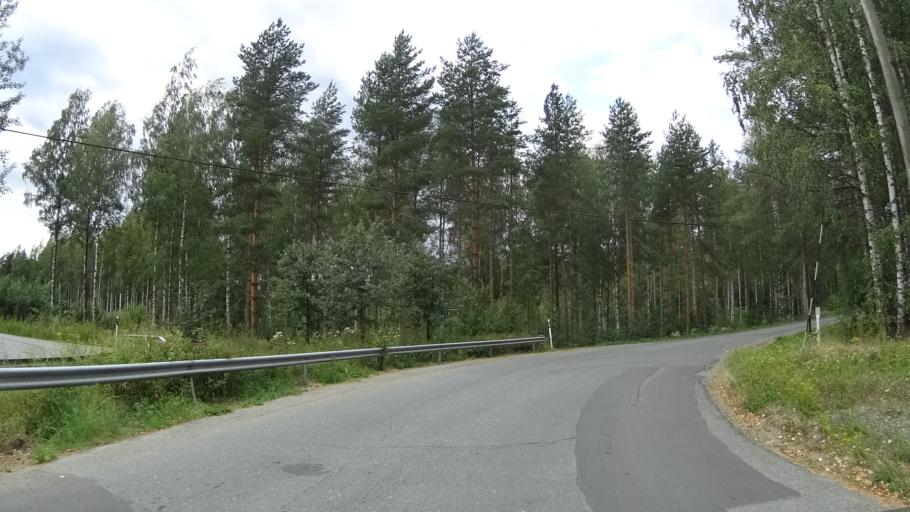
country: FI
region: Pirkanmaa
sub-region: Tampere
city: Kangasala
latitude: 61.4457
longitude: 24.1239
